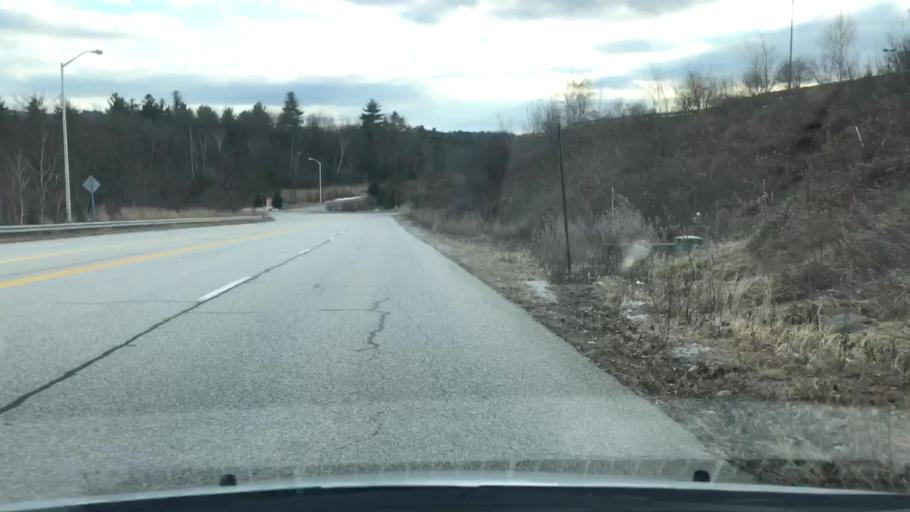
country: US
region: New Hampshire
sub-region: Merrimack County
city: South Hooksett
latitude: 43.0460
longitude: -71.4591
